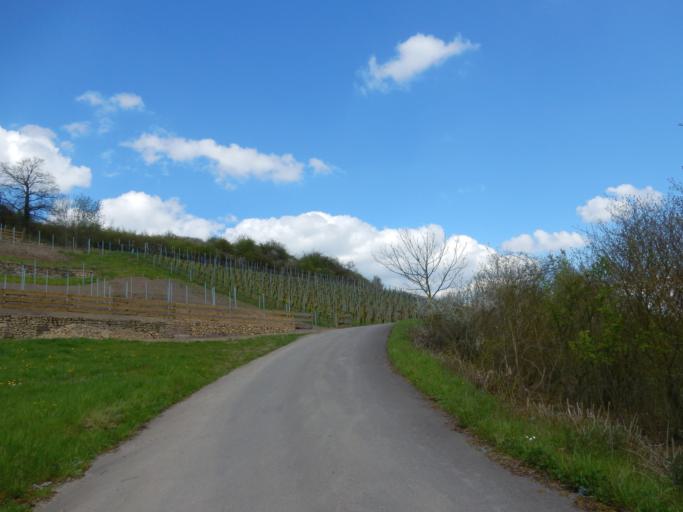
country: DE
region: Rheinland-Pfalz
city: Wellen
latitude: 49.6824
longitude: 6.4242
